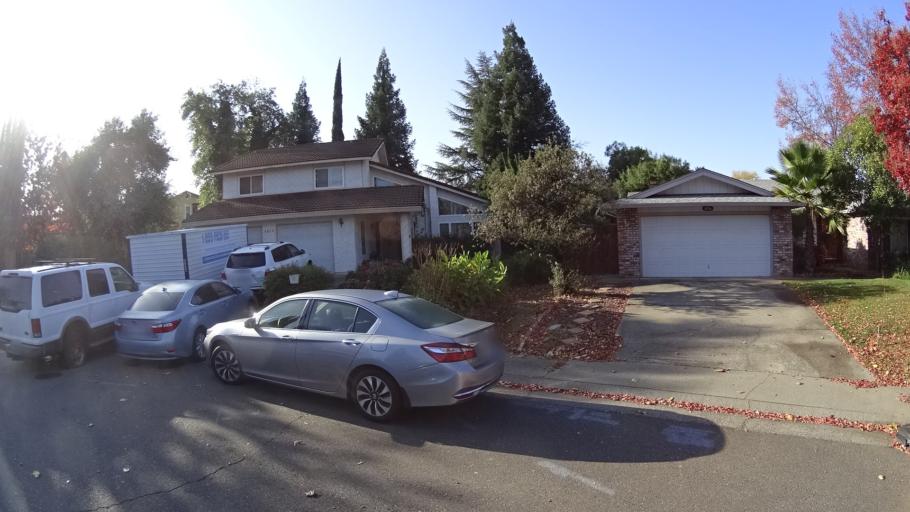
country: US
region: California
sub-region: Sacramento County
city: Citrus Heights
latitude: 38.6945
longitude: -121.2640
